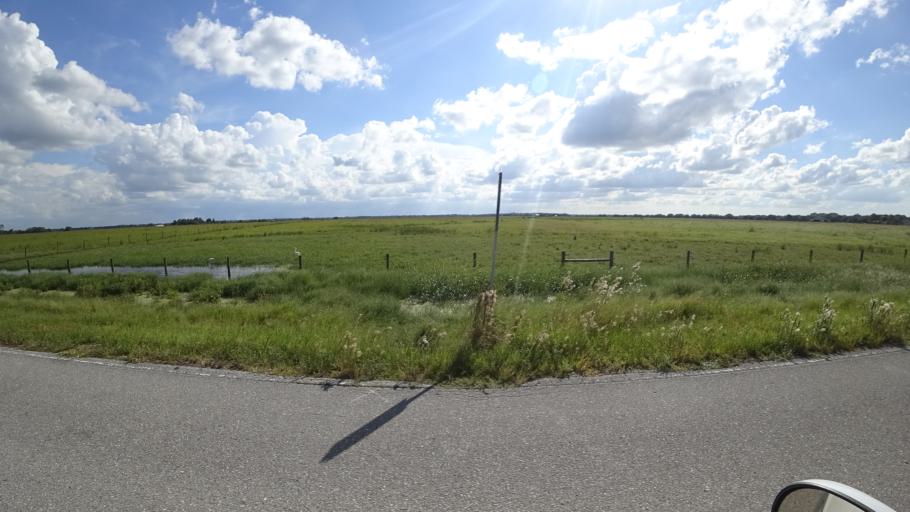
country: US
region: Florida
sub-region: DeSoto County
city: Nocatee
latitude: 27.2704
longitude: -82.0972
